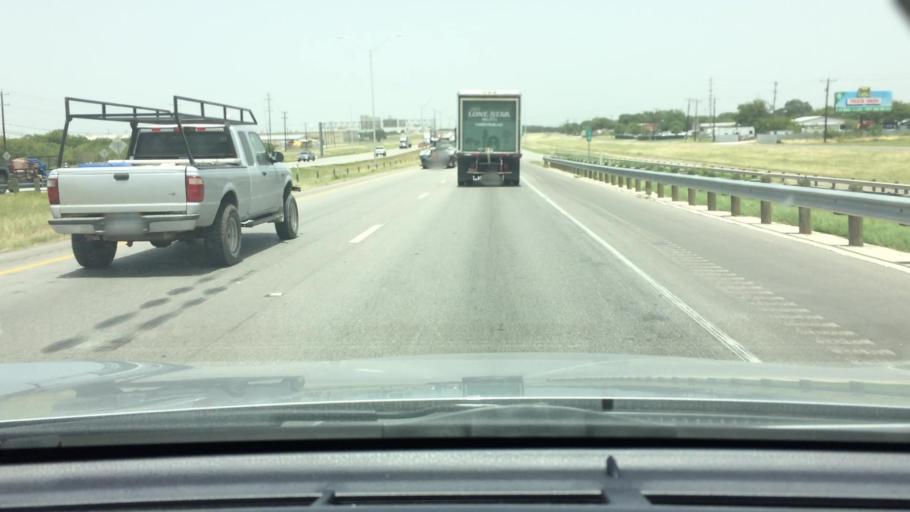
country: US
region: Texas
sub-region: Bexar County
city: Kirby
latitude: 29.4252
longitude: -98.3891
